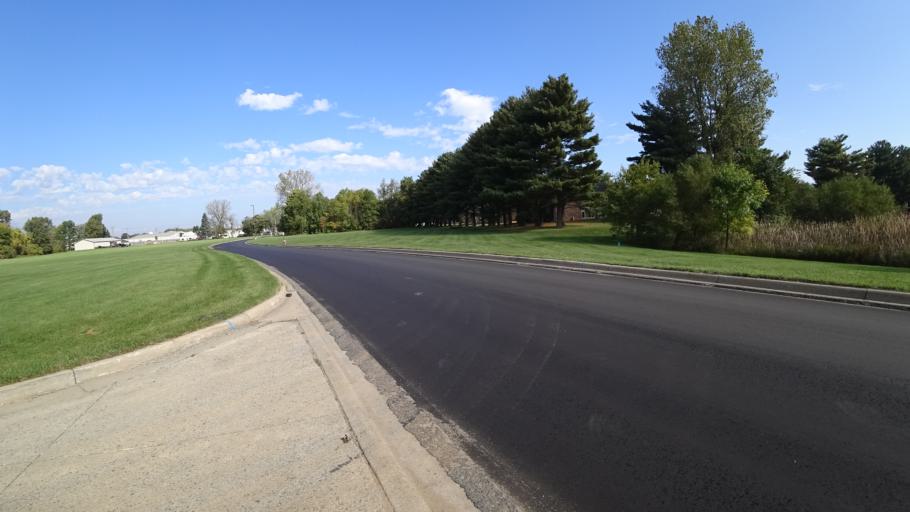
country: US
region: Michigan
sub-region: Saint Joseph County
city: Three Rivers
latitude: 41.9376
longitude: -85.6472
